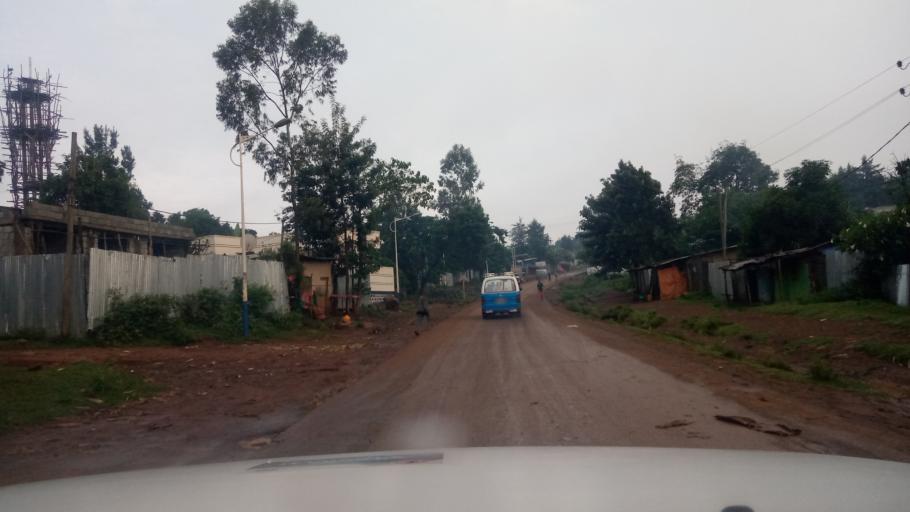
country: ET
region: Oromiya
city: Jima
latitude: 7.6943
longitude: 36.8188
